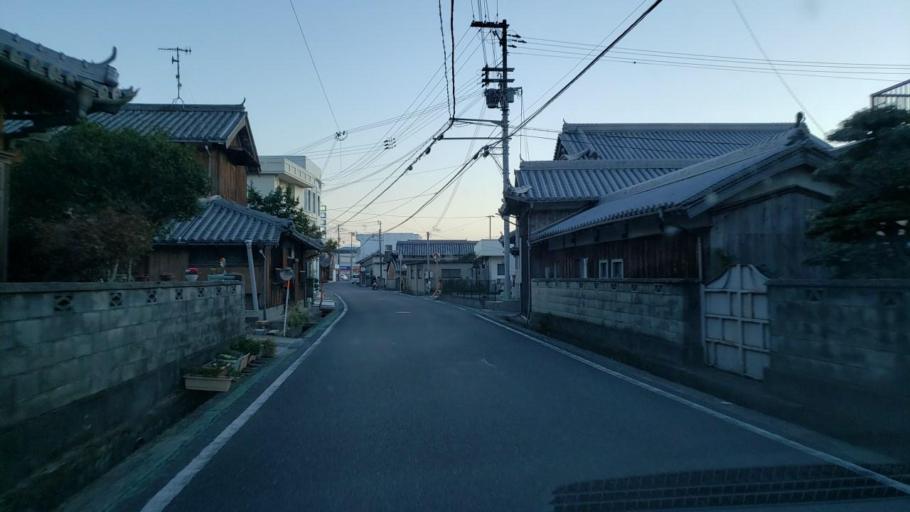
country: JP
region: Hyogo
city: Fukura
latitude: 34.3029
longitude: 134.7636
